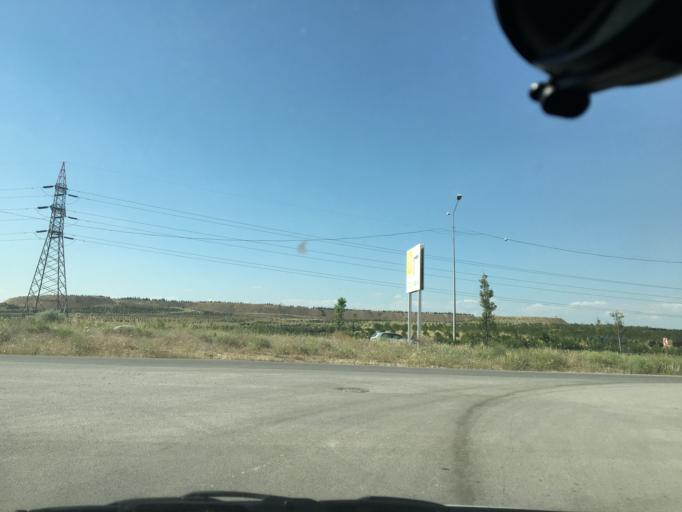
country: TR
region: Ankara
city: Batikent
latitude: 39.9120
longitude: 32.7432
